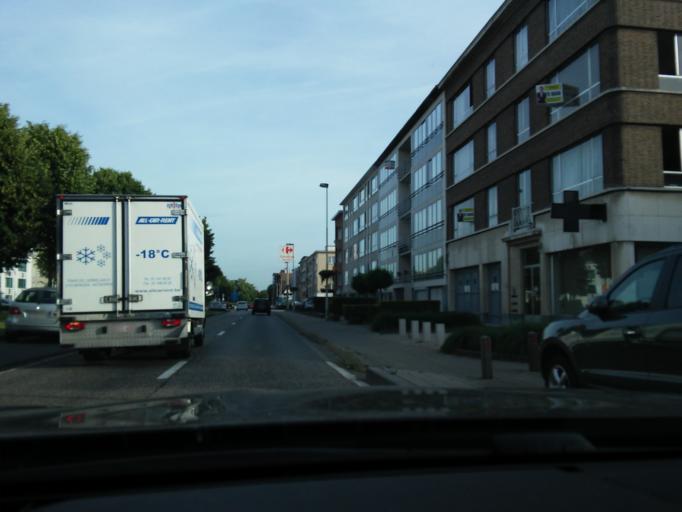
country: BE
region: Flanders
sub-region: Provincie Antwerpen
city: Edegem
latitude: 51.1758
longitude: 4.4248
